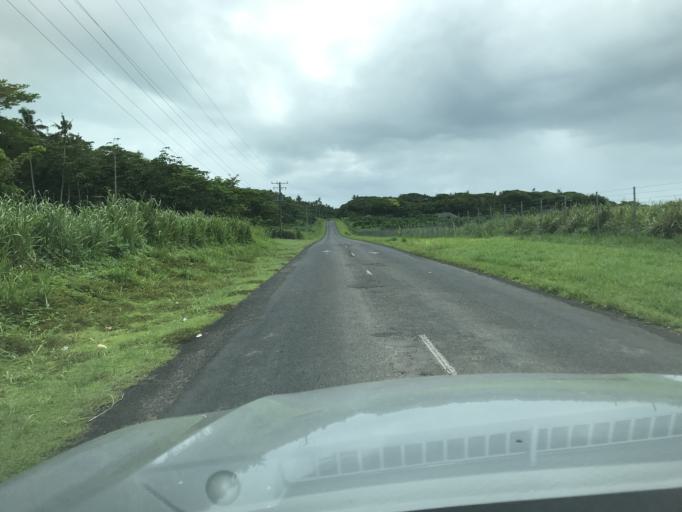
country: WS
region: Aiga-i-le-Tai
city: Mulifanua
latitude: -13.8339
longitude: -172.0111
